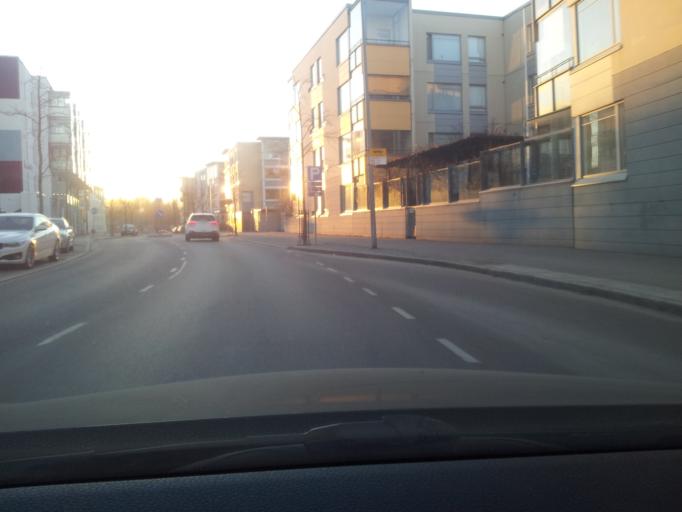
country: FI
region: Uusimaa
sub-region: Helsinki
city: Kilo
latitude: 60.2142
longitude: 24.8049
